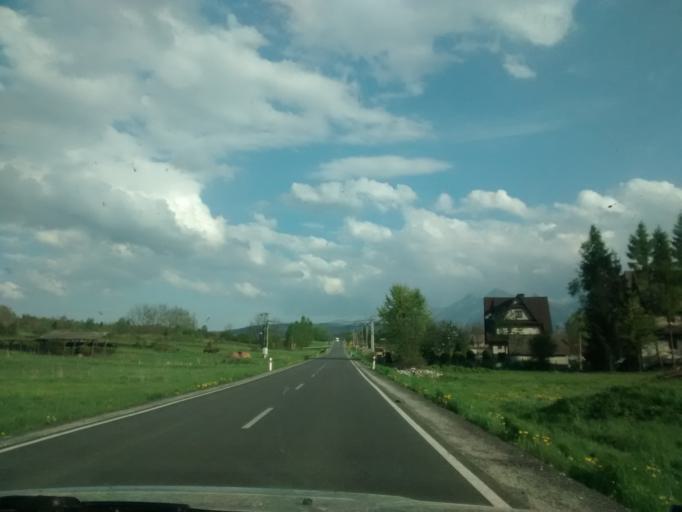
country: PL
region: Lesser Poland Voivodeship
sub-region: Powiat tatrzanski
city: Bukowina Tatrzanska
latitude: 49.3445
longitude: 20.1379
